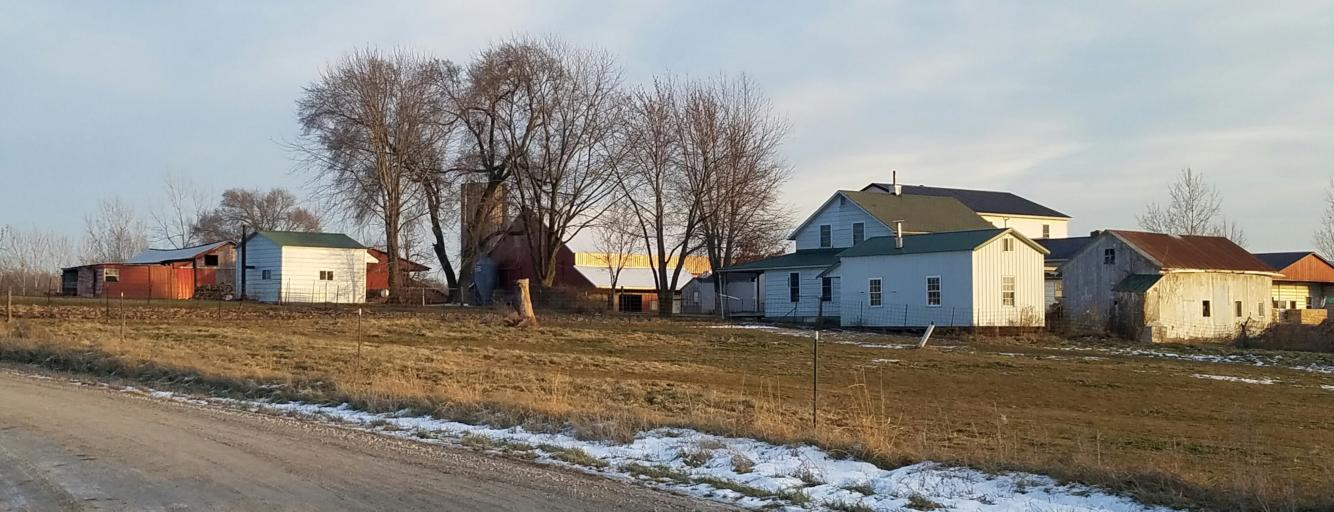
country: US
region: Missouri
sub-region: Randolph County
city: Moberly
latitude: 39.3187
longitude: -92.3038
